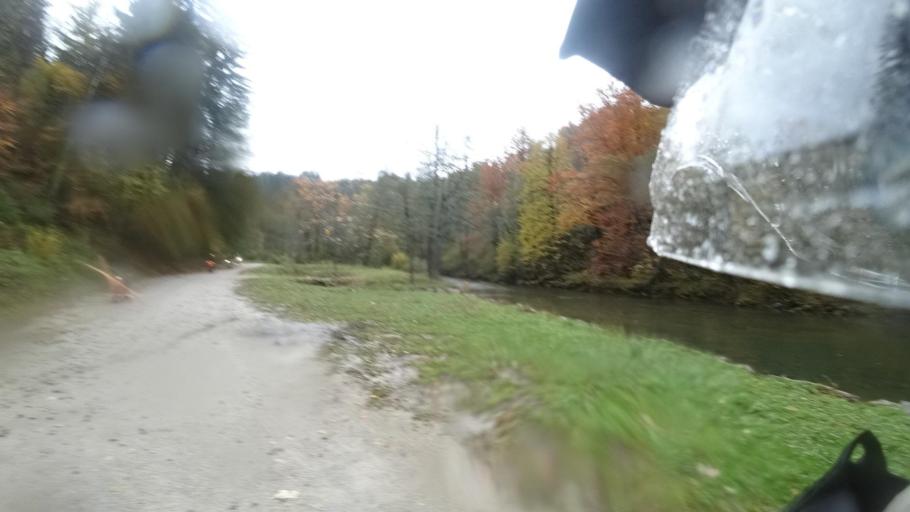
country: HR
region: Primorsko-Goranska
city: Vrbovsko
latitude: 45.3648
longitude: 15.0751
